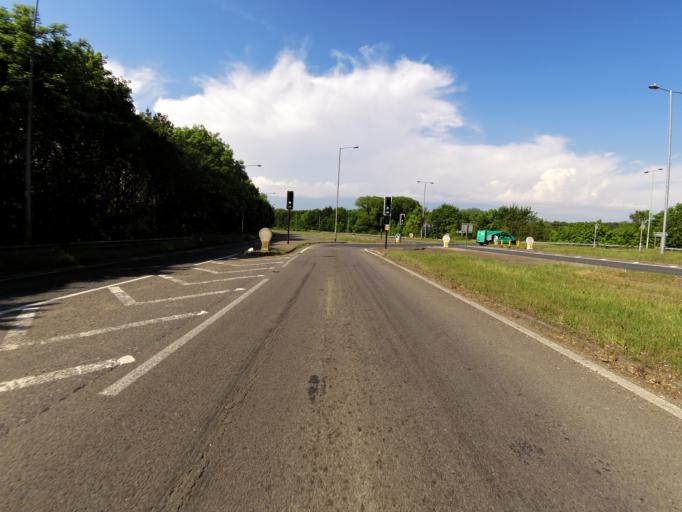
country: GB
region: England
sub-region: Suffolk
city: Bramford
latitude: 52.1028
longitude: 1.0987
